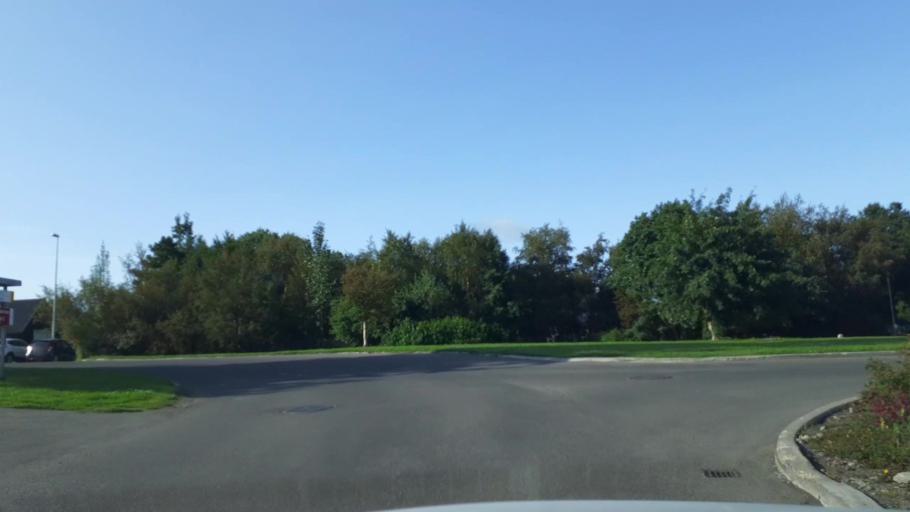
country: IS
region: Northeast
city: Akureyri
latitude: 65.6740
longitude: -18.0945
